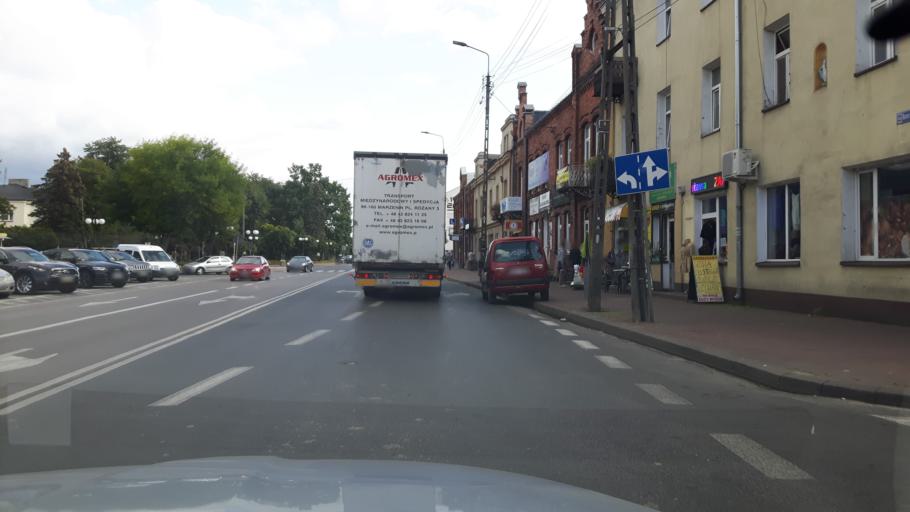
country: PL
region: Masovian Voivodeship
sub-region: Powiat wolominski
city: Radzymin
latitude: 52.4171
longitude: 21.1815
